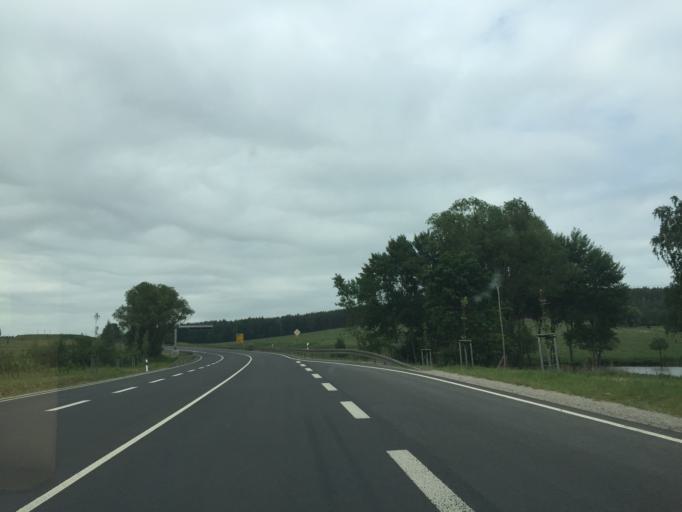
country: DE
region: Thuringia
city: Langewiesen
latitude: 50.6770
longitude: 10.9858
